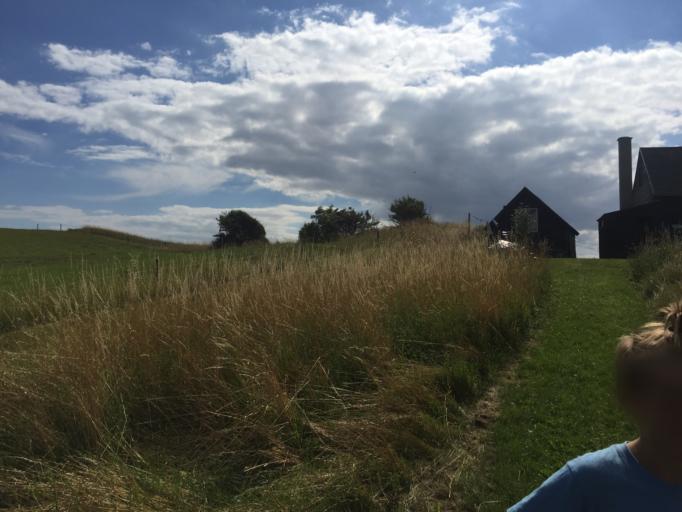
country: DK
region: South Denmark
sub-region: Faaborg-Midtfyn Kommune
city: Faaborg
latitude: 55.0665
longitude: 10.2370
